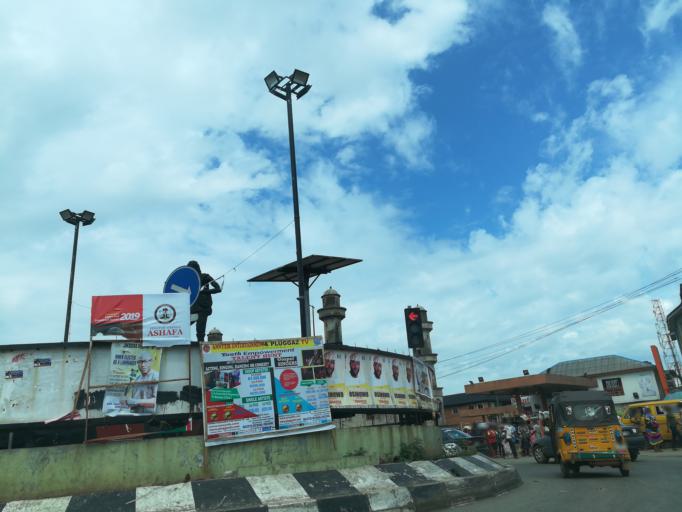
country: NG
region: Lagos
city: Ikorodu
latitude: 6.6204
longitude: 3.5034
